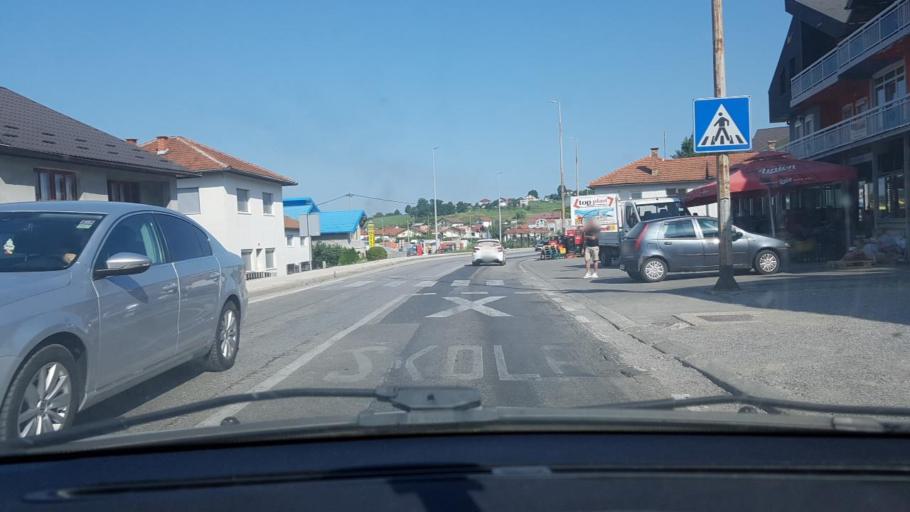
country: BA
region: Federation of Bosnia and Herzegovina
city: Coralici
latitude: 44.9802
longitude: 15.8908
